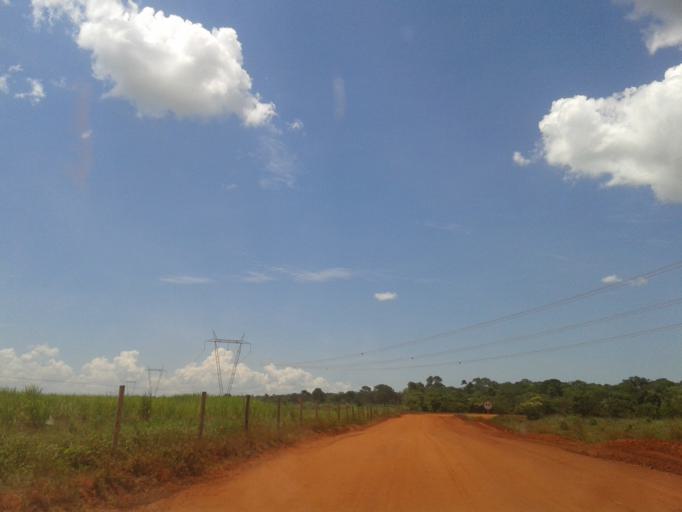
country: BR
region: Minas Gerais
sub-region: Santa Vitoria
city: Santa Vitoria
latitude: -19.1630
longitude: -50.4076
